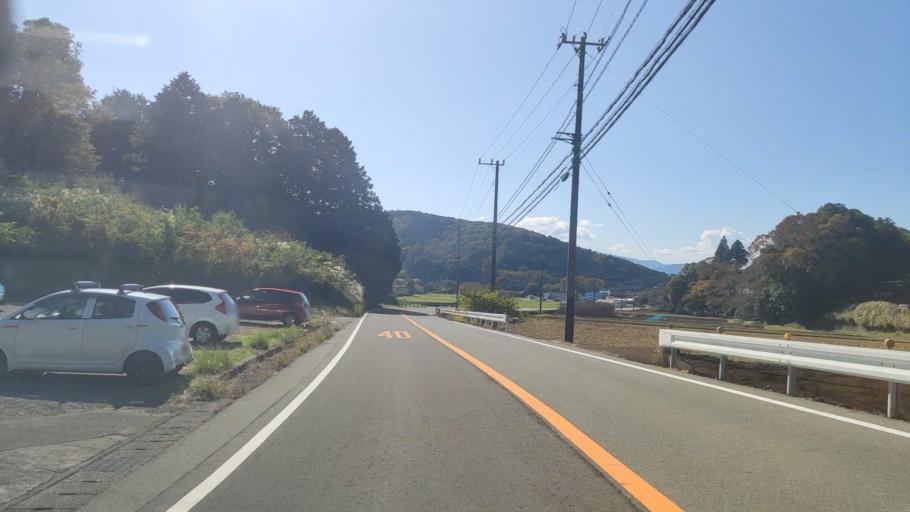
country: JP
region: Shizuoka
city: Atami
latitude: 35.0203
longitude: 139.0094
